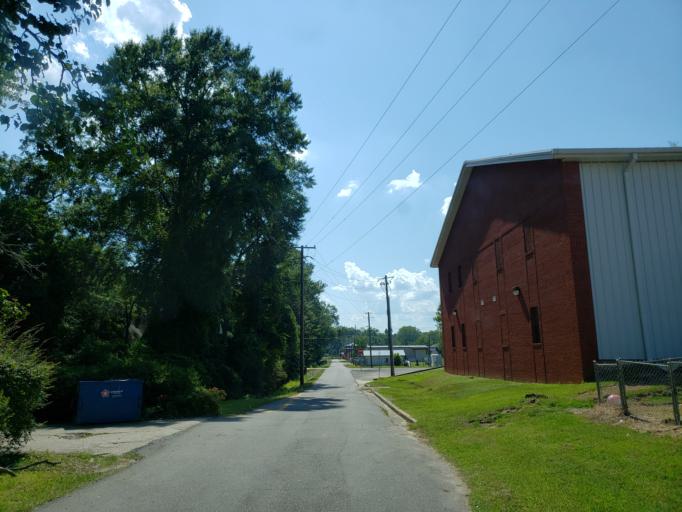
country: US
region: Mississippi
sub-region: Lamar County
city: Sumrall
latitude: 31.4166
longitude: -89.5426
